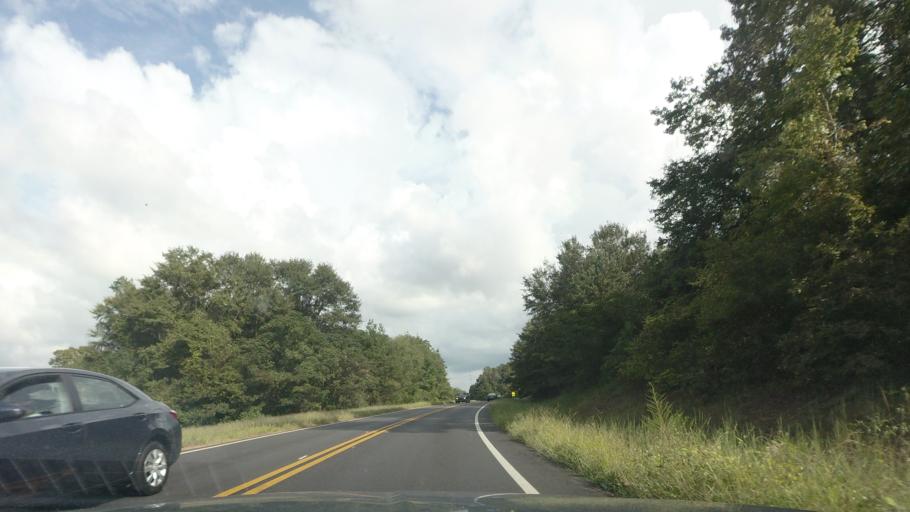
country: US
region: Georgia
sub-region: Houston County
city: Centerville
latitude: 32.6346
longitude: -83.7124
